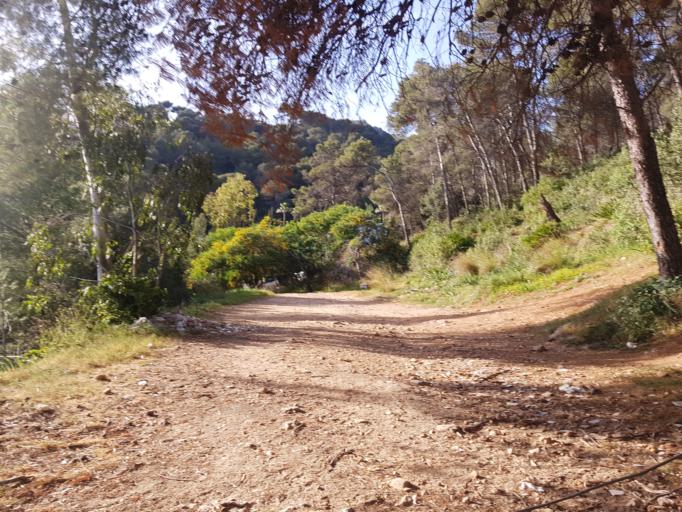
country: ES
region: Andalusia
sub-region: Provincia de Malaga
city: Marbella
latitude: 36.5298
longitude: -4.8843
